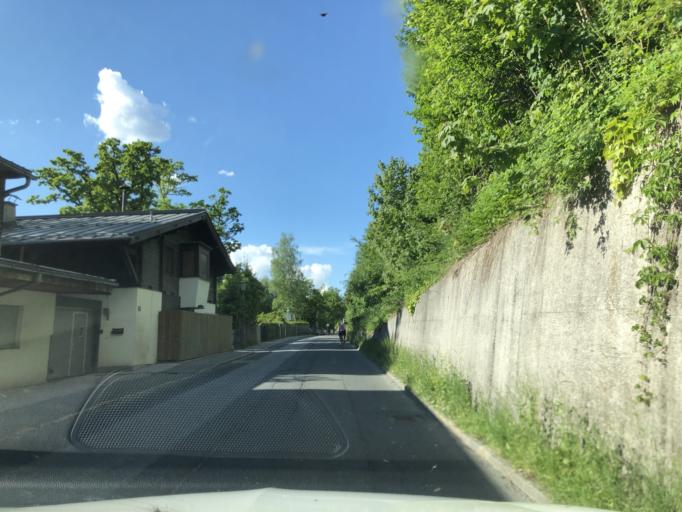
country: AT
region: Salzburg
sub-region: Politischer Bezirk Zell am See
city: Zell am See
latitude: 47.3223
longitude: 12.8161
